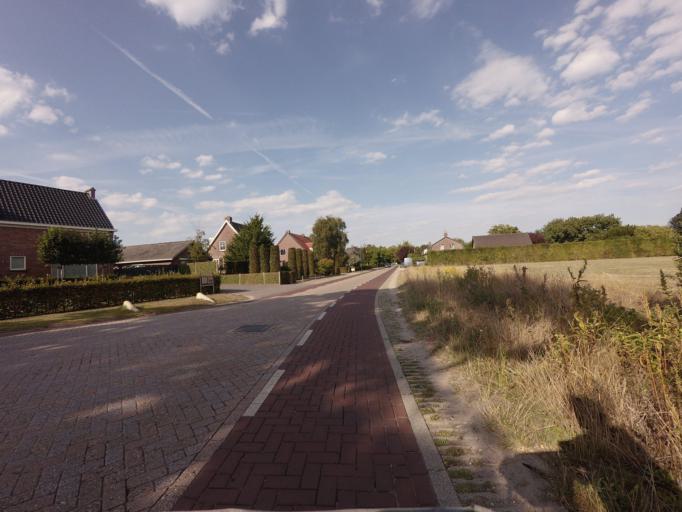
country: NL
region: North Brabant
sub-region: Gemeente Heeze-Leende
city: Heeze
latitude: 51.3433
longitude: 5.5479
